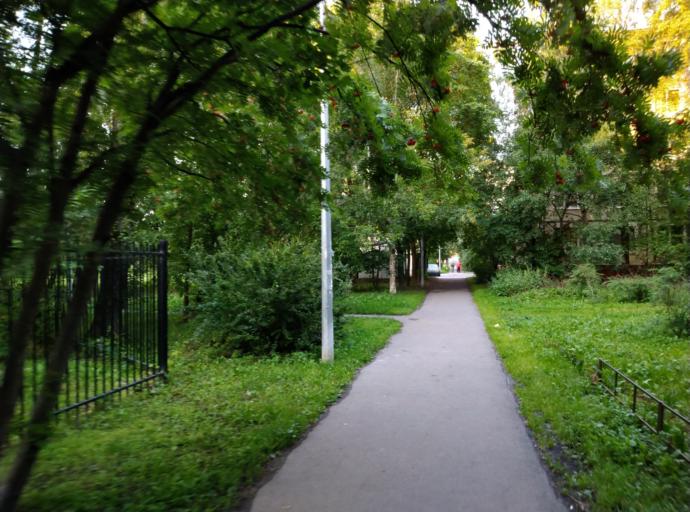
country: RU
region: St.-Petersburg
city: Kupchino
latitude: 59.8559
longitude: 30.3410
